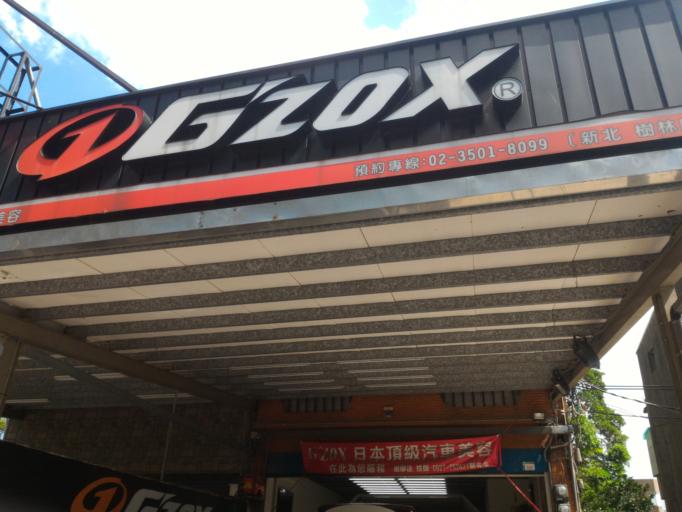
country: TW
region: Taiwan
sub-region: Taoyuan
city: Taoyuan
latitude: 24.9479
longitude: 121.3853
